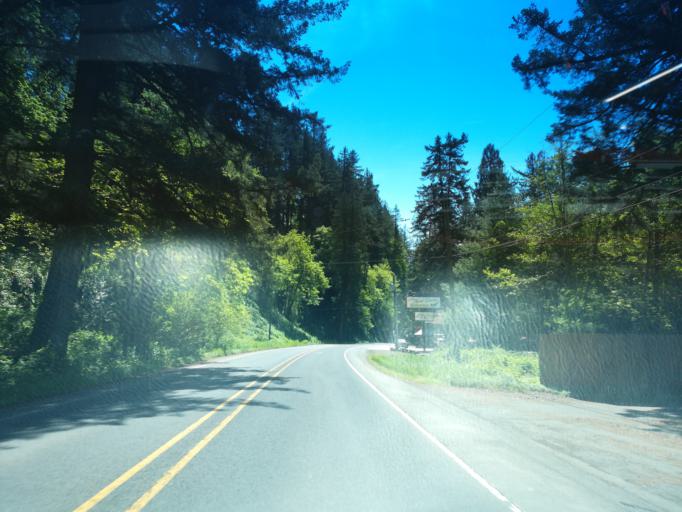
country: US
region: Oregon
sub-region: Multnomah County
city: Troutdale
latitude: 45.5173
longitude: -122.3686
